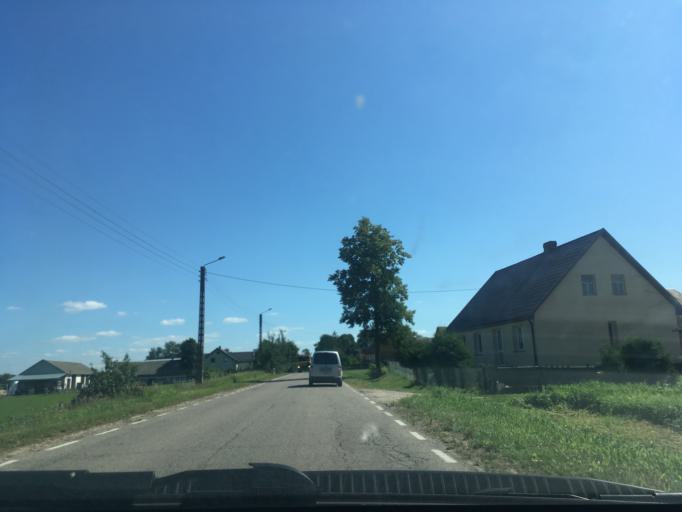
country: PL
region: Podlasie
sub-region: Powiat suwalski
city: Raczki
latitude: 53.9636
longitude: 22.8149
